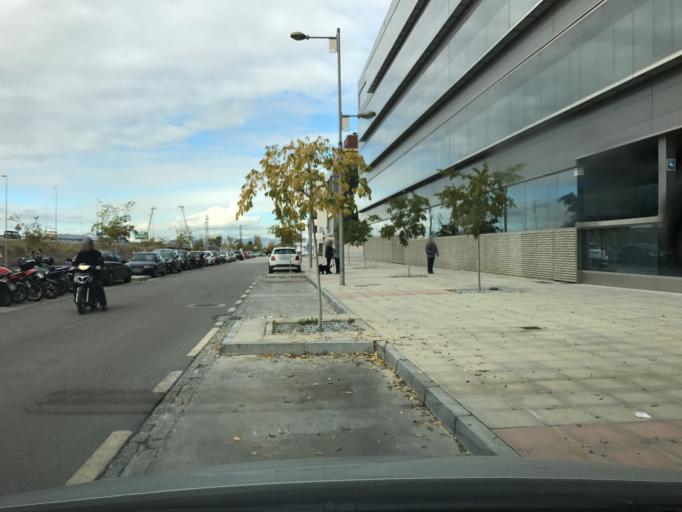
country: ES
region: Andalusia
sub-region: Provincia de Granada
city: Armilla
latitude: 37.1501
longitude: -3.6107
